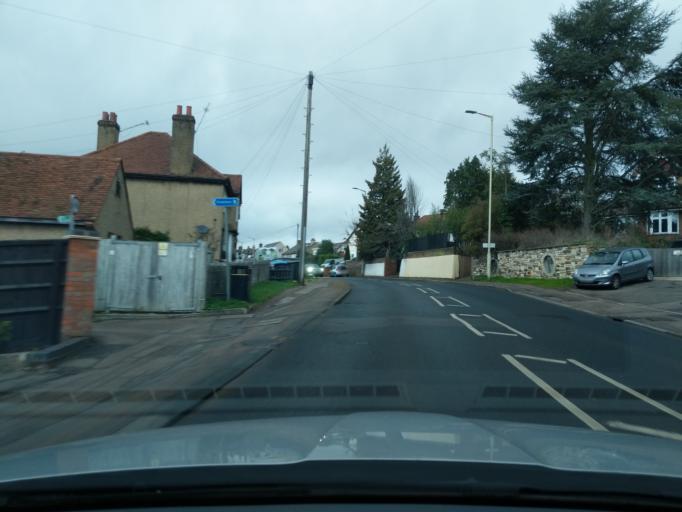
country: GB
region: England
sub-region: Hertfordshire
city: Hemel Hempstead
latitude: 51.7365
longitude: -0.4612
